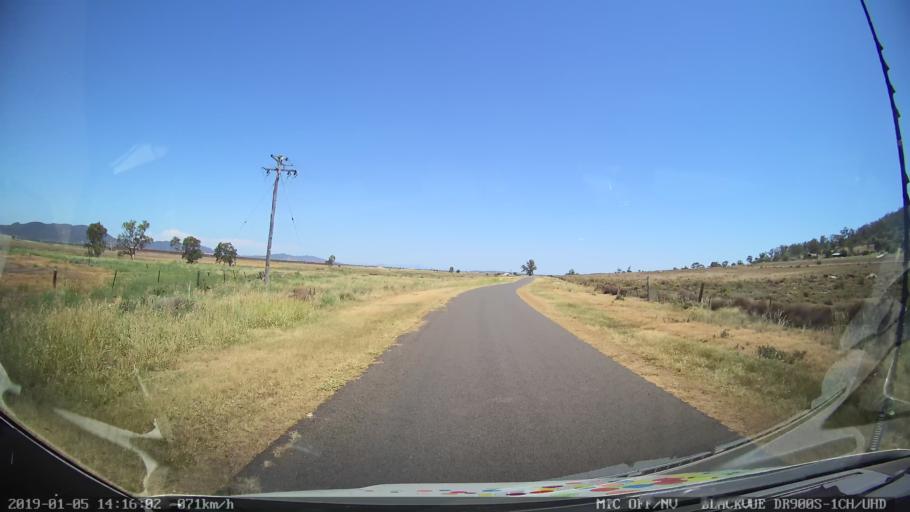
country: AU
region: New South Wales
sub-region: Liverpool Plains
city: Quirindi
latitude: -31.2528
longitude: 150.4722
